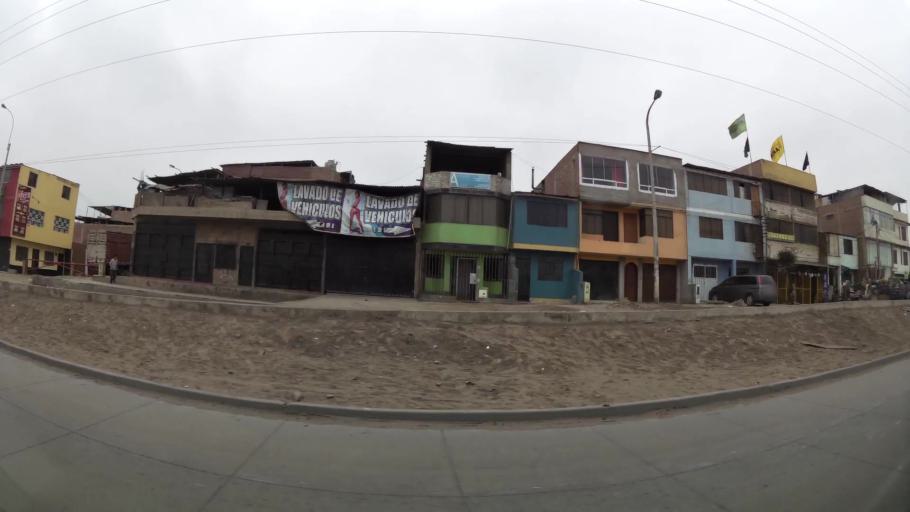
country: PE
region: Lima
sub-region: Lima
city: Surco
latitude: -12.2065
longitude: -76.9518
